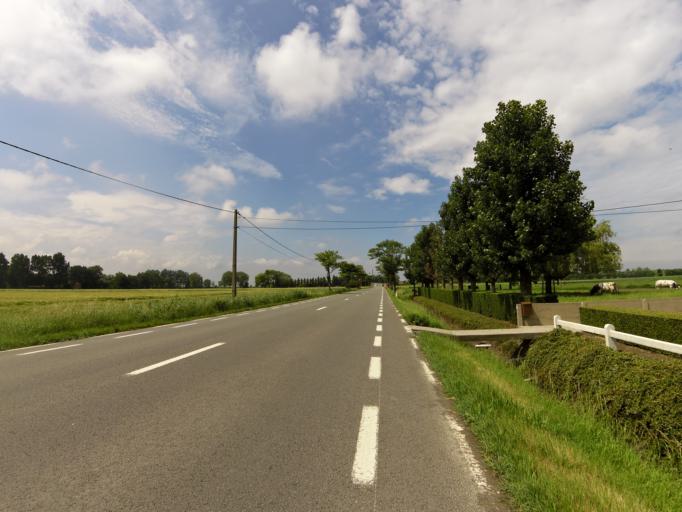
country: BE
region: Flanders
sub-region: Provincie West-Vlaanderen
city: Nieuwpoort
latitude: 51.1264
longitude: 2.8093
